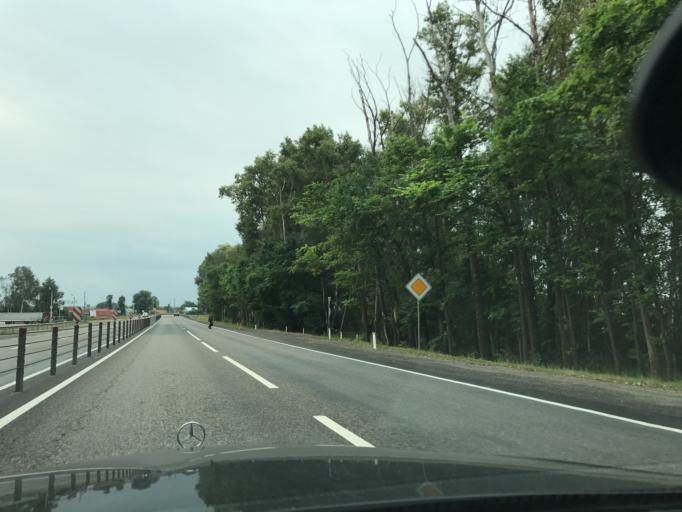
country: RU
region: Vladimir
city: Novovyazniki
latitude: 56.1761
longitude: 42.4148
